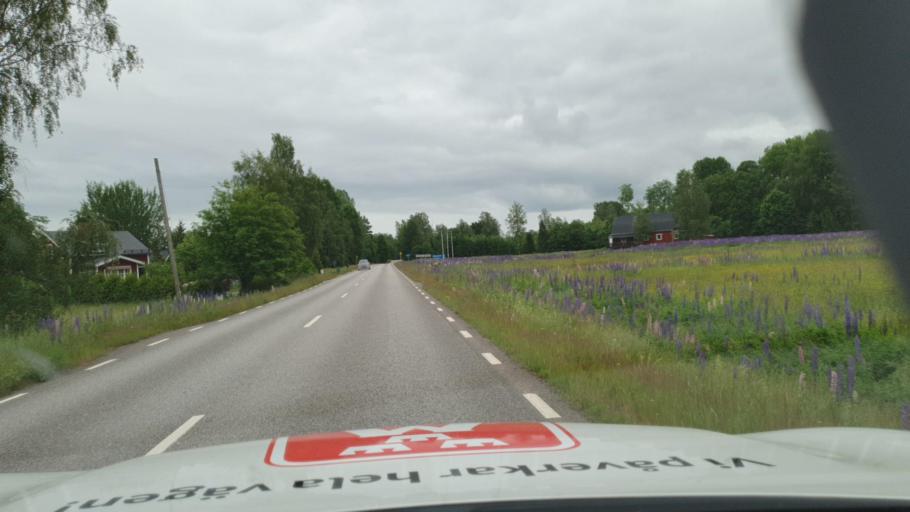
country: SE
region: Vaermland
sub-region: Sunne Kommun
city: Sunne
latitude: 59.8061
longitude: 13.0375
